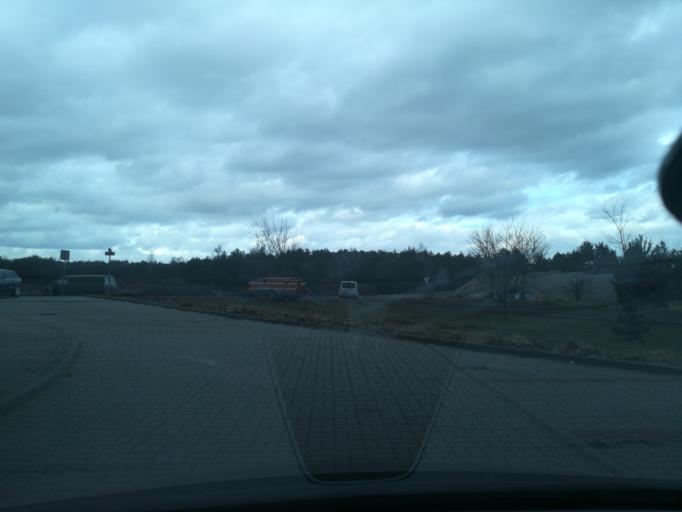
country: PL
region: Kujawsko-Pomorskie
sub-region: Powiat torunski
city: Lubicz Dolny
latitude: 52.9833
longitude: 18.6848
